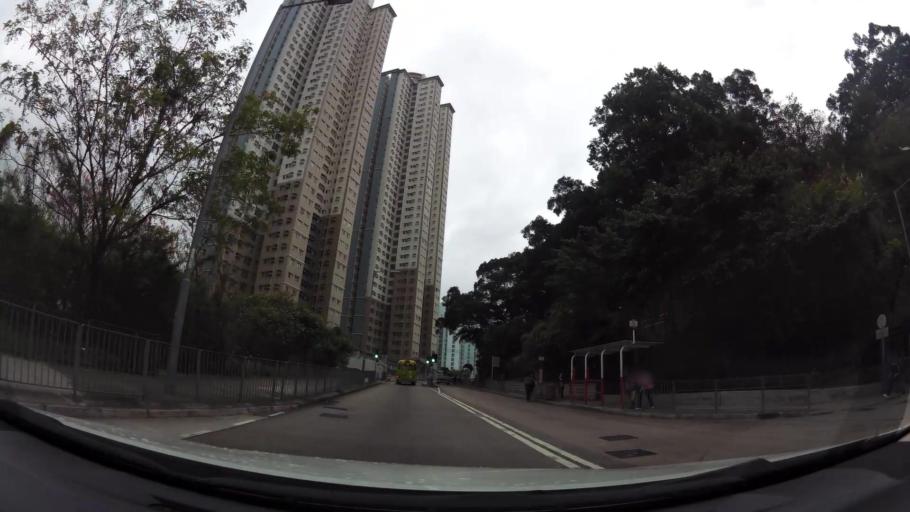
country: HK
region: Tsuen Wan
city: Tsuen Wan
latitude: 22.3638
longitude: 114.1230
